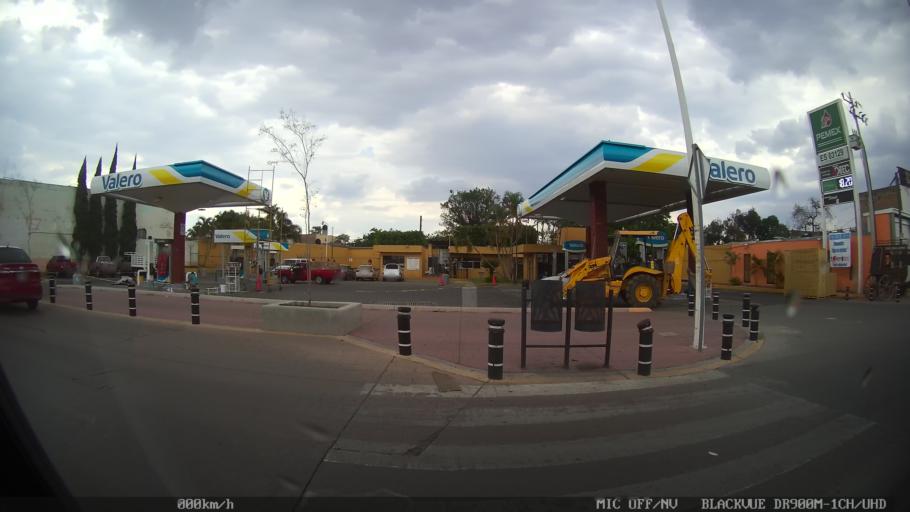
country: MX
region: Jalisco
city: Tonala
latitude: 20.6191
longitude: -103.2462
